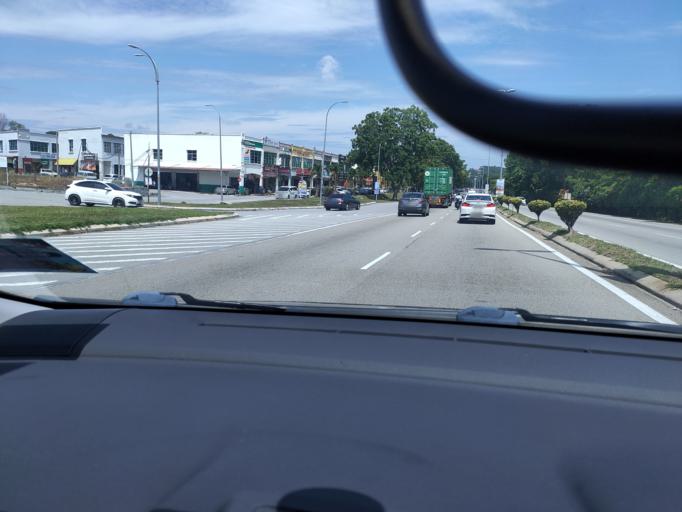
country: MY
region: Melaka
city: Bukit Rambai
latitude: 2.2733
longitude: 102.2162
